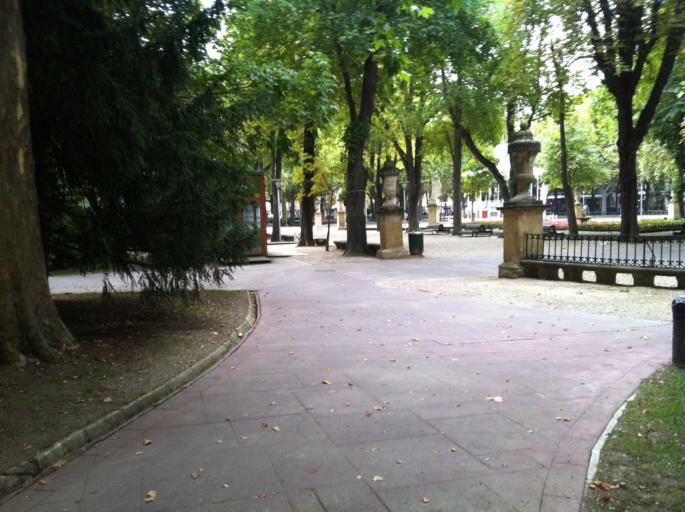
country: ES
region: Basque Country
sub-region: Provincia de Alava
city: Gasteiz / Vitoria
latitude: 42.8446
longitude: -2.6772
